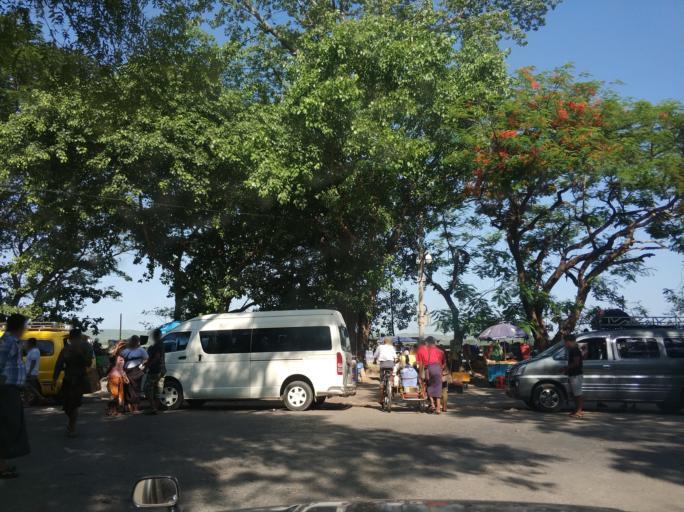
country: MM
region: Mandalay
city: Mandalay
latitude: 21.9715
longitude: 96.0567
